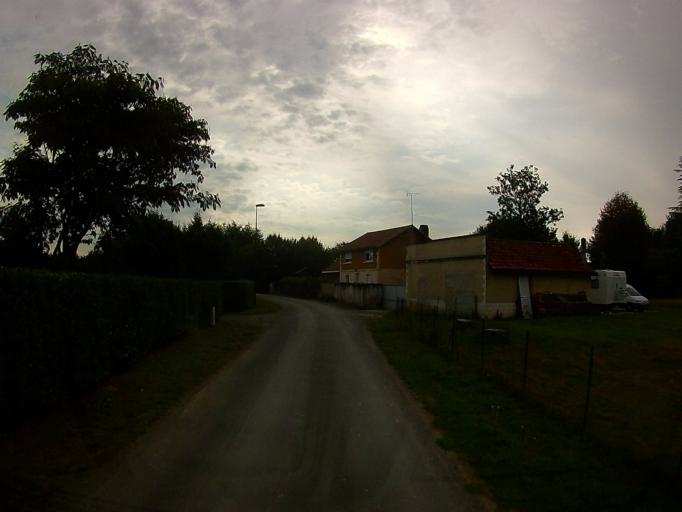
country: FR
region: Aquitaine
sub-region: Departement de la Dordogne
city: Chancelade
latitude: 45.1924
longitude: 0.6226
